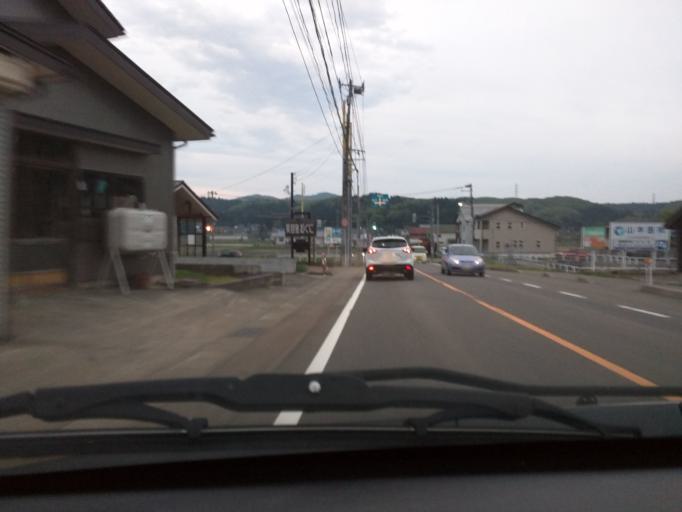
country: JP
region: Niigata
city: Ojiya
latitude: 37.3202
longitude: 138.7187
